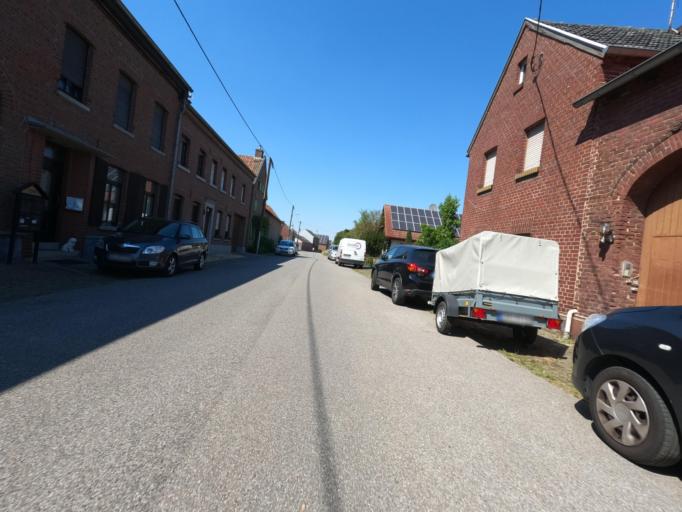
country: DE
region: North Rhine-Westphalia
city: Erkelenz
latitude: 51.0943
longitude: 6.3000
